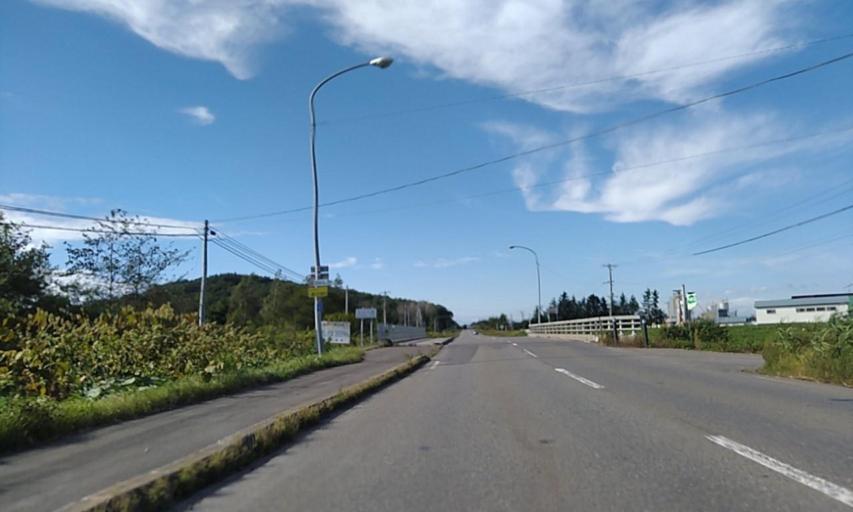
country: JP
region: Hokkaido
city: Obihiro
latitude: 42.8300
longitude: 143.4694
